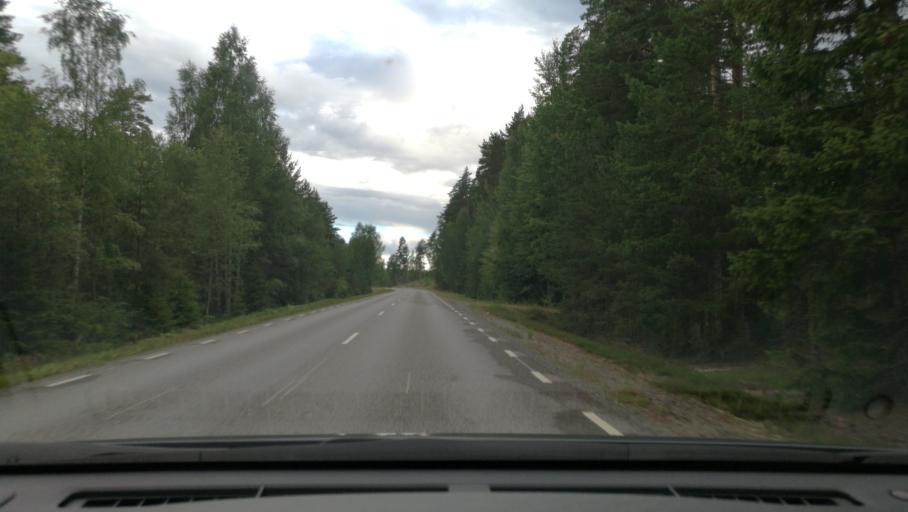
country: SE
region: OEstergoetland
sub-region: Norrkopings Kommun
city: Svartinge
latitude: 58.7418
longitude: 15.9644
